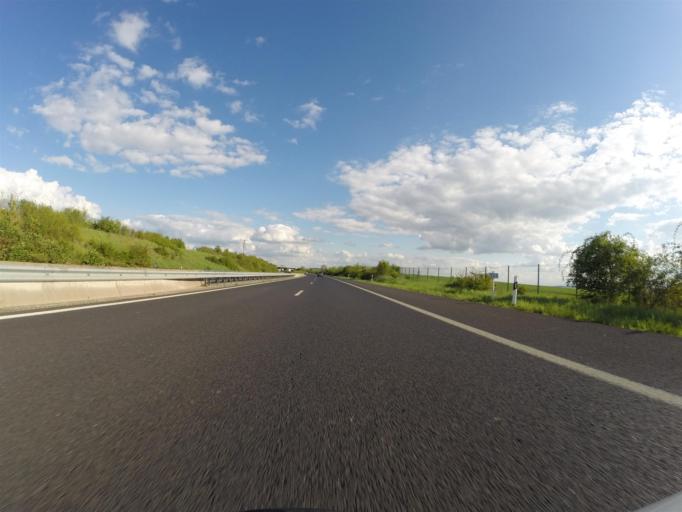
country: LU
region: Grevenmacher
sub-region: Canton de Remich
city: Mondorf-les-Bains
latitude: 49.5027
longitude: 6.3052
